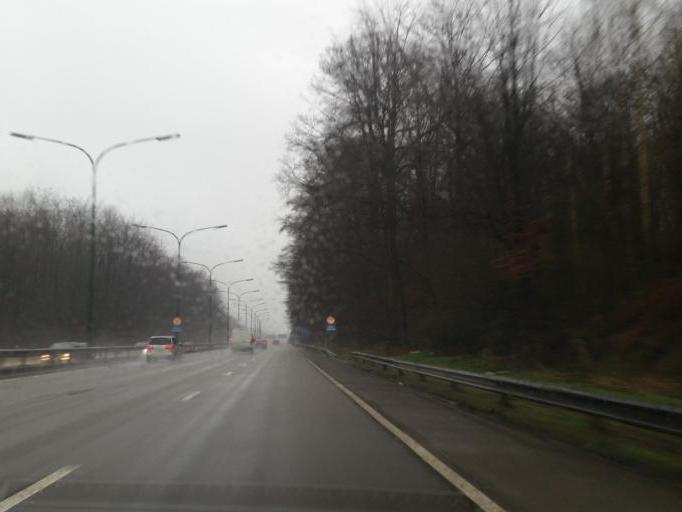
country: BE
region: Flanders
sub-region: Provincie Vlaams-Brabant
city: Hoeilaart
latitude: 50.8060
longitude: 4.4528
